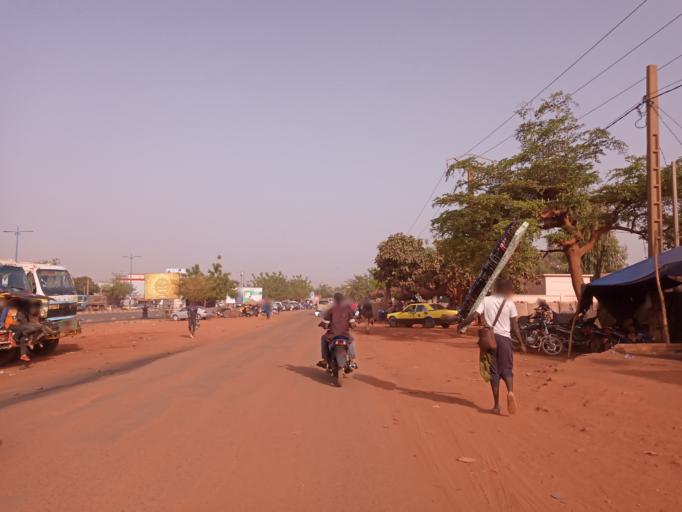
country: ML
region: Bamako
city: Bamako
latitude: 12.6001
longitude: -7.9632
